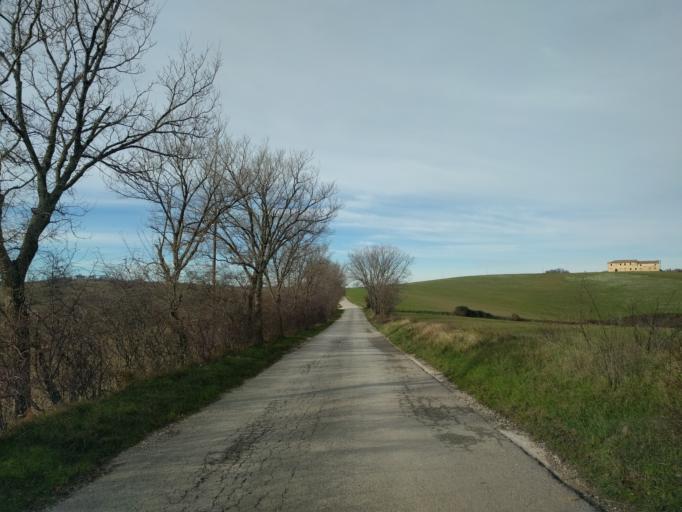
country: IT
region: The Marches
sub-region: Provincia di Pesaro e Urbino
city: Cuccurano
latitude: 43.8088
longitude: 12.9408
